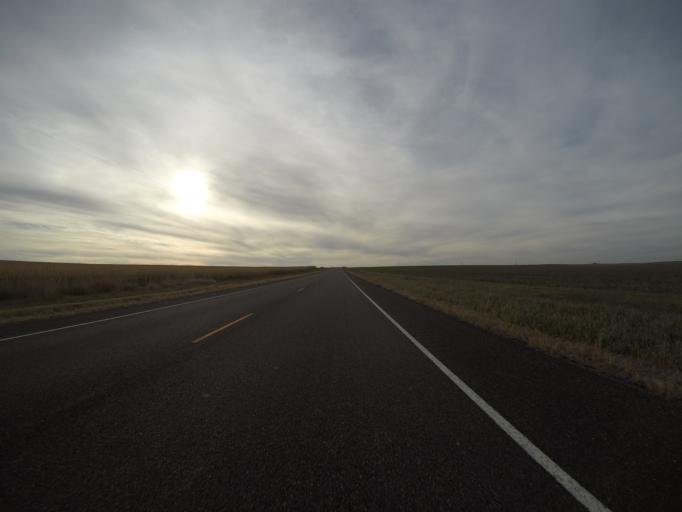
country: US
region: Kansas
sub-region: Cheyenne County
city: Saint Francis
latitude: 39.7460
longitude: -102.1325
